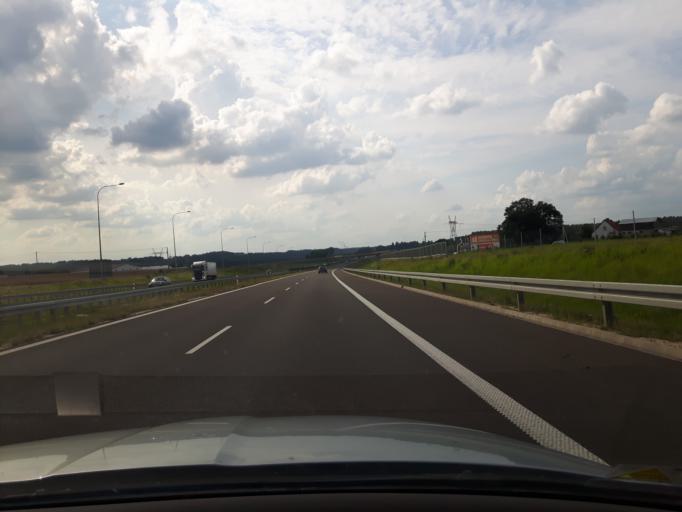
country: PL
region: Warmian-Masurian Voivodeship
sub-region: Powiat ostrodzki
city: Gierzwald
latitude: 53.5957
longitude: 20.0922
